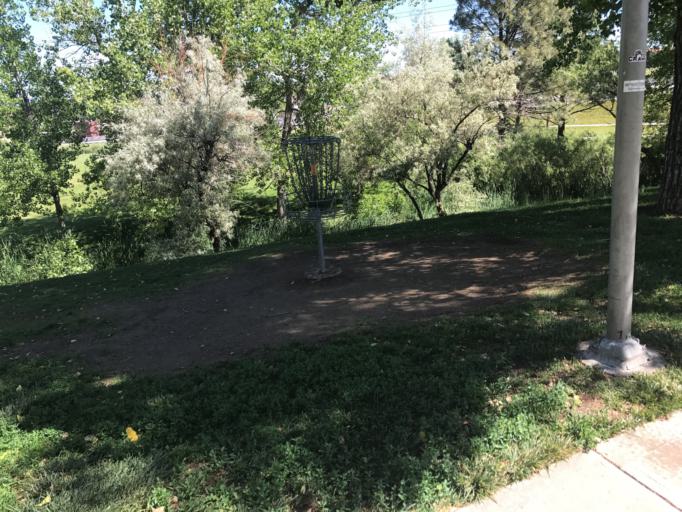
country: US
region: Colorado
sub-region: Broomfield County
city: Broomfield
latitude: 39.9209
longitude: -105.1070
